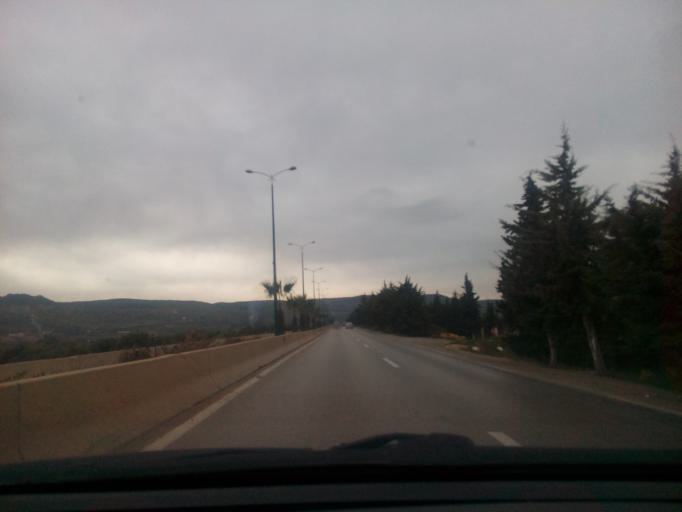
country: DZ
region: Tlemcen
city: Mansoura
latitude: 34.8754
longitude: -1.3493
